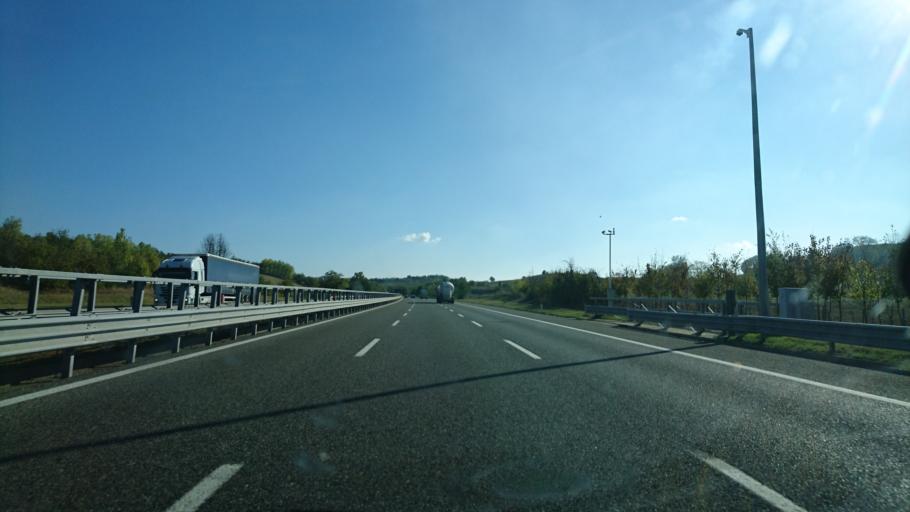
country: IT
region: Piedmont
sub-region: Provincia di Alessandria
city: Mirabello Monferrato
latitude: 45.0143
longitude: 8.5350
